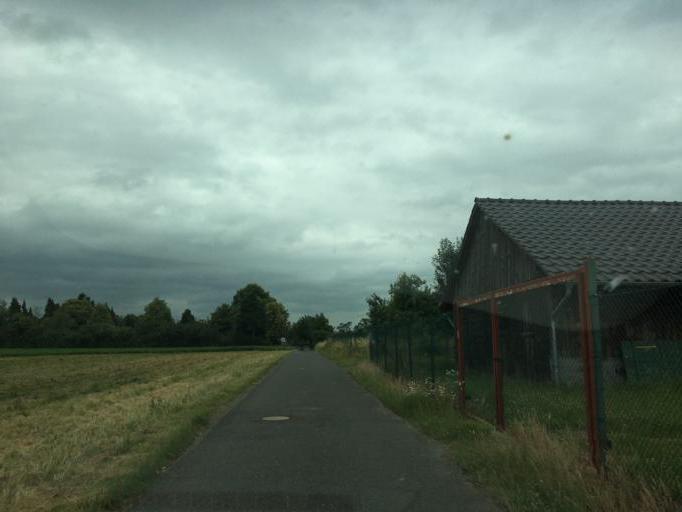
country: DE
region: North Rhine-Westphalia
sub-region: Regierungsbezirk Koln
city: Merzenich
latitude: 50.7953
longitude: 6.5435
